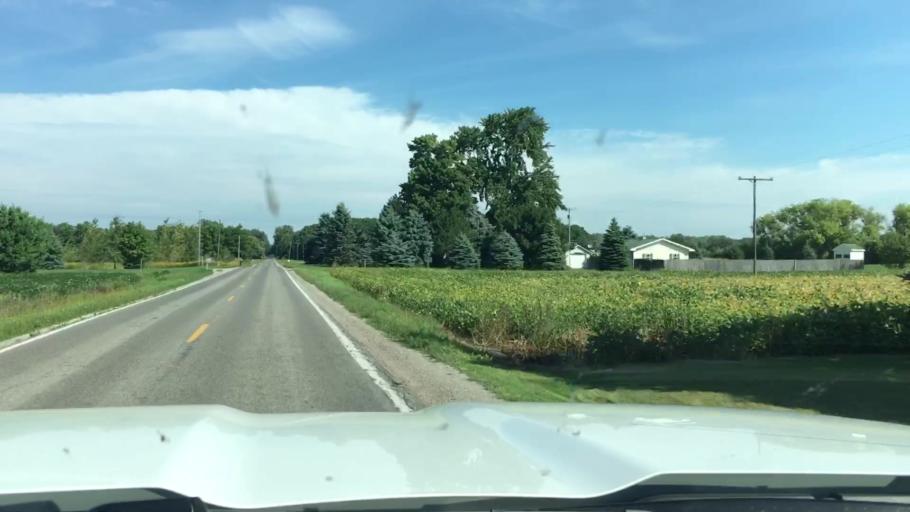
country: US
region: Michigan
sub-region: Saginaw County
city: Hemlock
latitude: 43.4546
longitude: -84.2302
